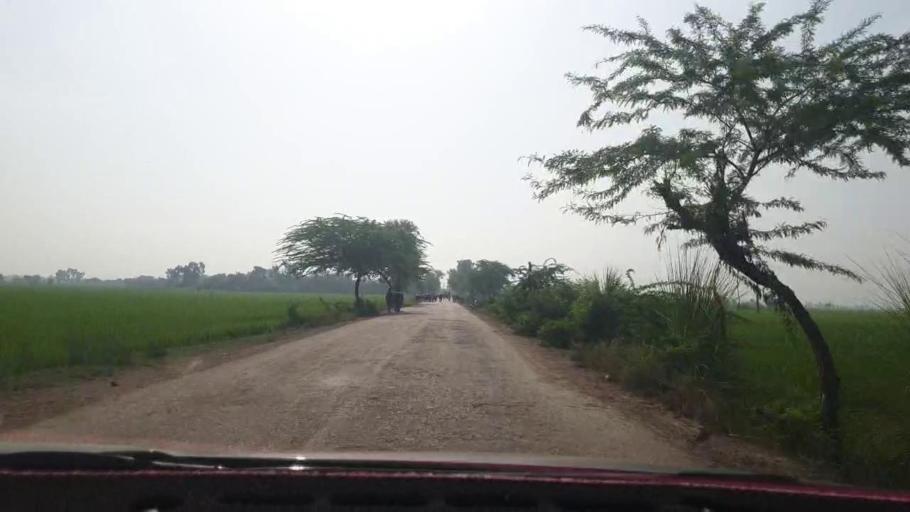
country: PK
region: Sindh
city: Nasirabad
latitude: 27.4407
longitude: 67.9505
